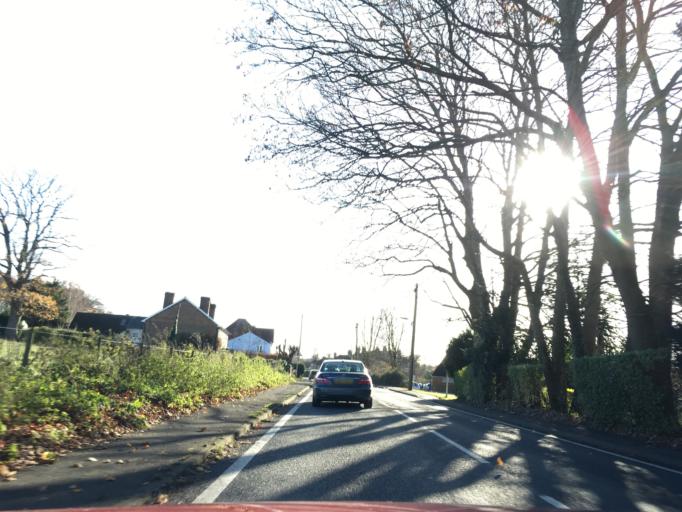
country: GB
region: England
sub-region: Hampshire
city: Colden Common
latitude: 51.0013
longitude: -1.3172
